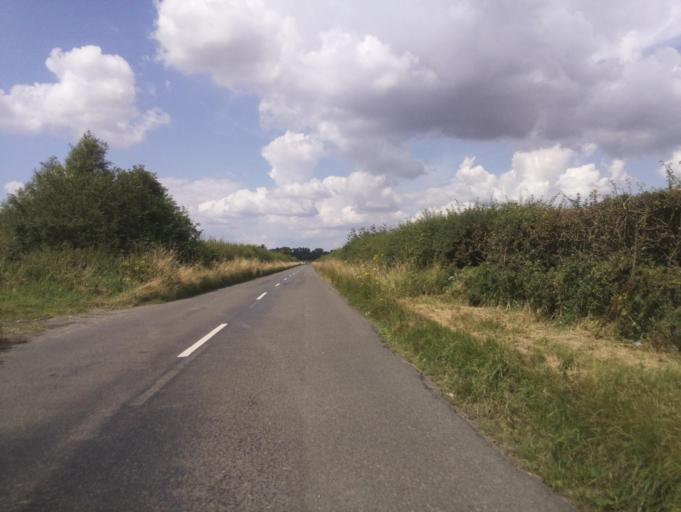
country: GB
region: England
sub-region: Borough of Swindon
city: Bishopstone
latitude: 51.5754
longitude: -1.6374
